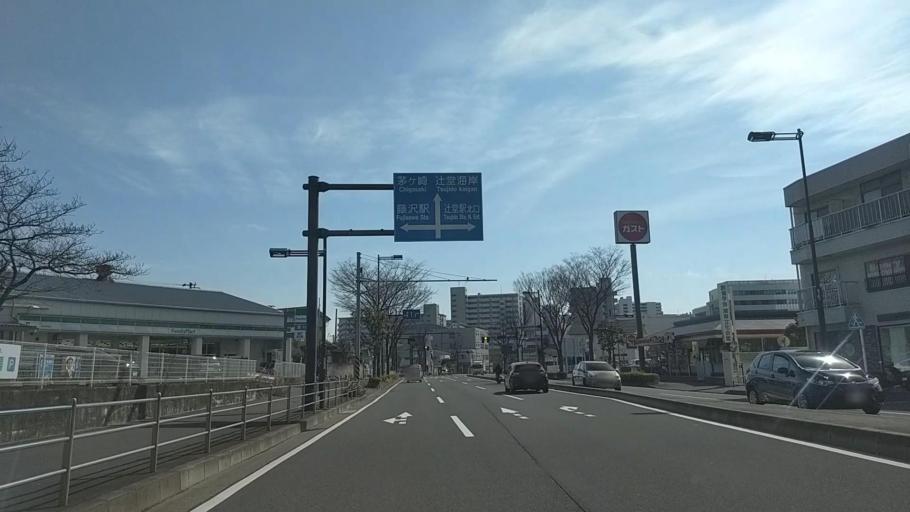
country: JP
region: Kanagawa
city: Fujisawa
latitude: 35.3425
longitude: 139.4491
